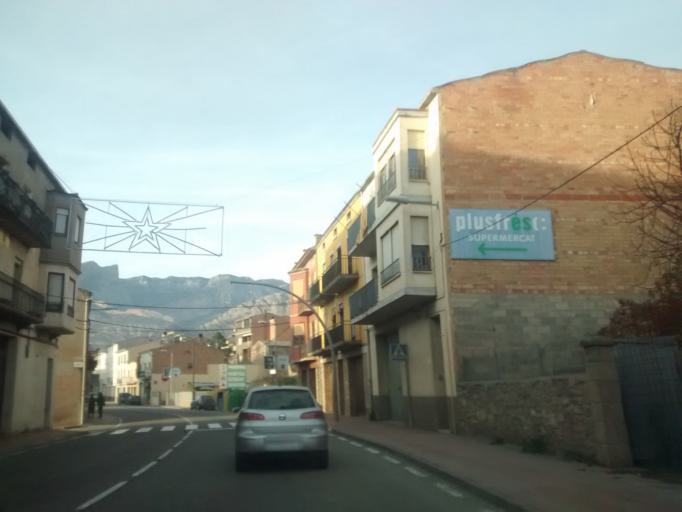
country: ES
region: Catalonia
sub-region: Provincia de Lleida
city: Oliana
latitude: 42.0699
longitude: 1.3127
